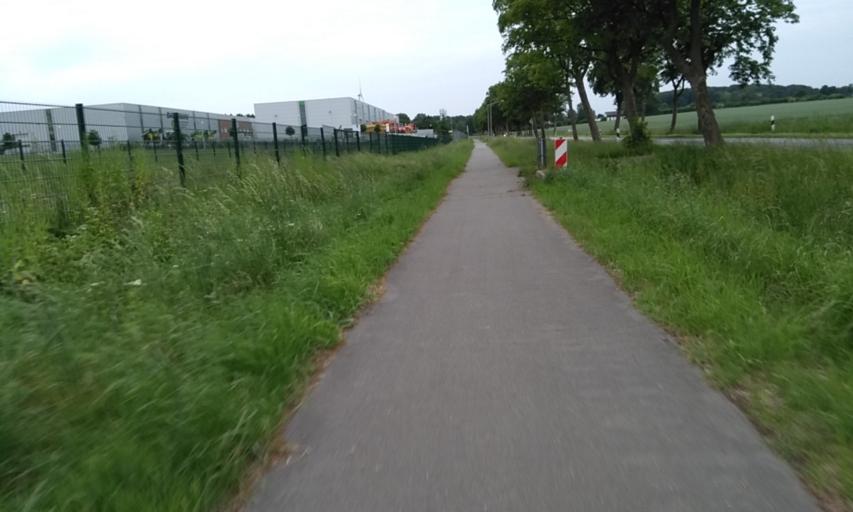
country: DE
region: Lower Saxony
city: Nottensdorf
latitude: 53.4737
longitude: 9.6044
